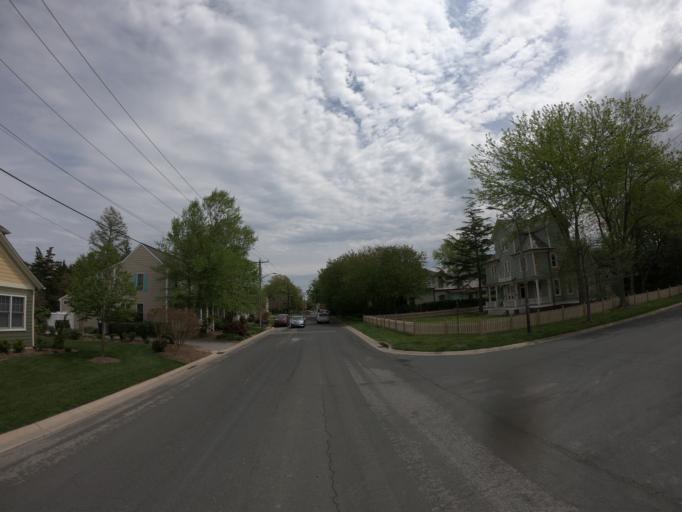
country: US
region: Delaware
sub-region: Sussex County
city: Lewes
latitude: 38.7773
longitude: -75.1451
